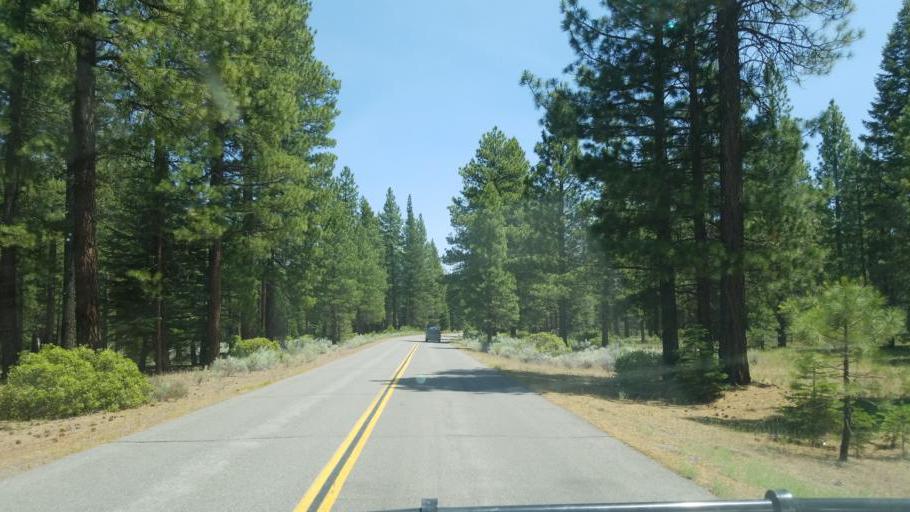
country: US
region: California
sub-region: Lassen County
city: Susanville
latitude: 40.5467
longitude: -120.8039
